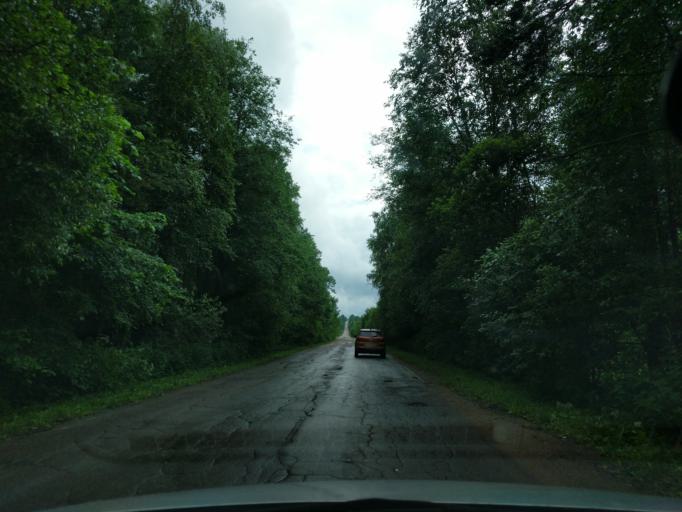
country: RU
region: Kaluga
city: Nikola-Lenivets
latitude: 54.7623
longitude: 35.7053
